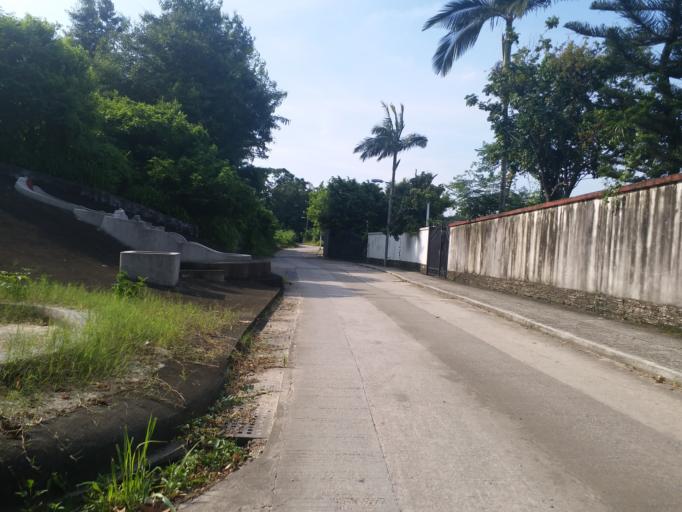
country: HK
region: Yuen Long
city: Yuen Long Kau Hui
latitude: 22.4446
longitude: 114.0113
